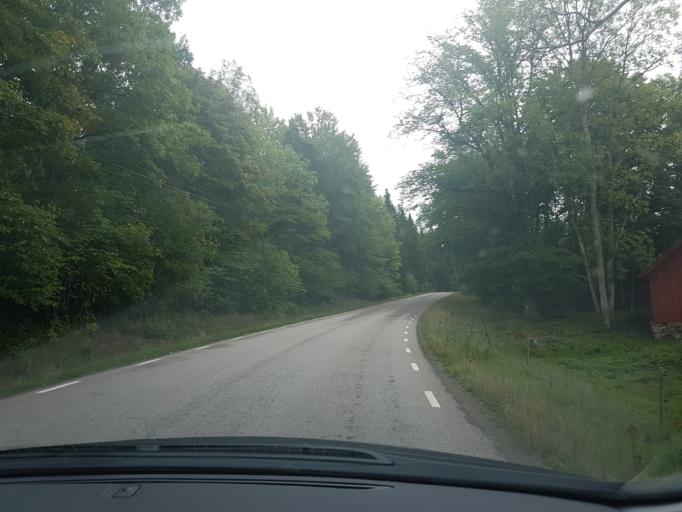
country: SE
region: Joenkoeping
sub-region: Vetlanda Kommun
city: Vetlanda
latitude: 57.3181
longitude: 15.1302
